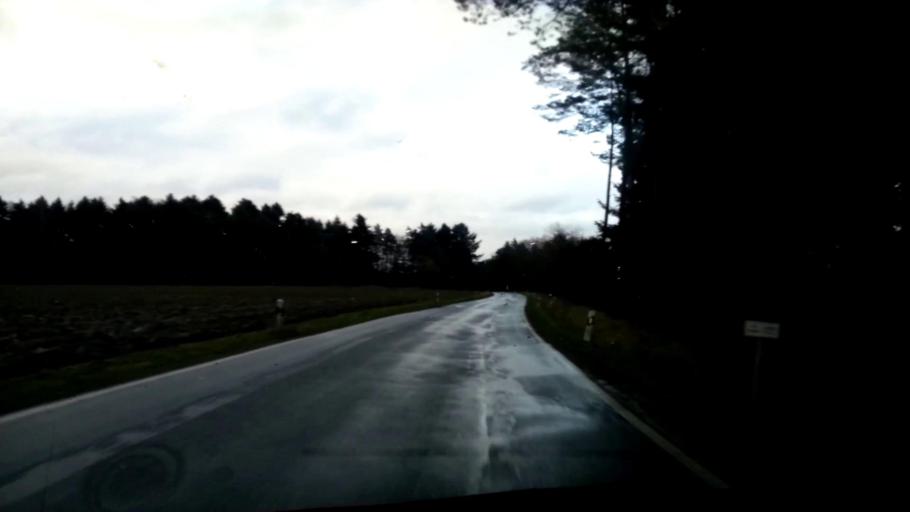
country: DE
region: Bavaria
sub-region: Upper Franconia
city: Konigsfeld
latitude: 49.9266
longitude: 11.1875
